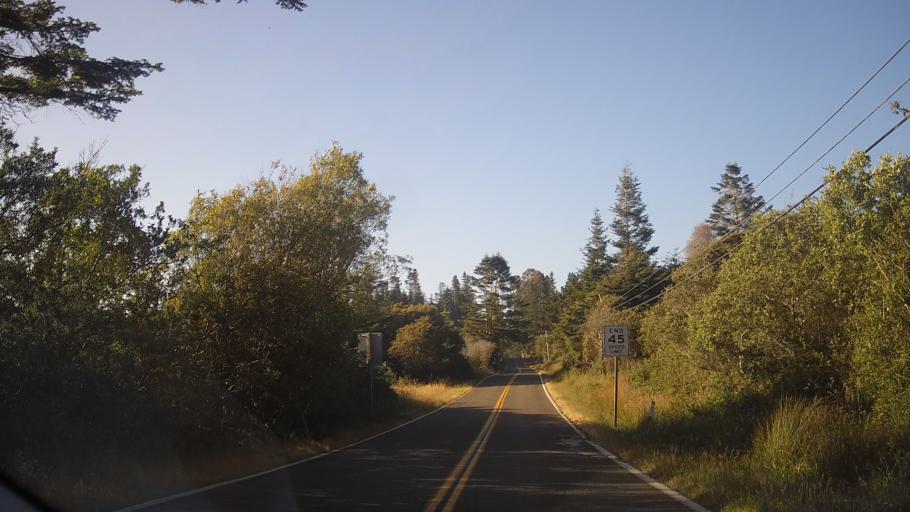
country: US
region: California
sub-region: Mendocino County
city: Fort Bragg
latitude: 39.5123
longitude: -123.7644
